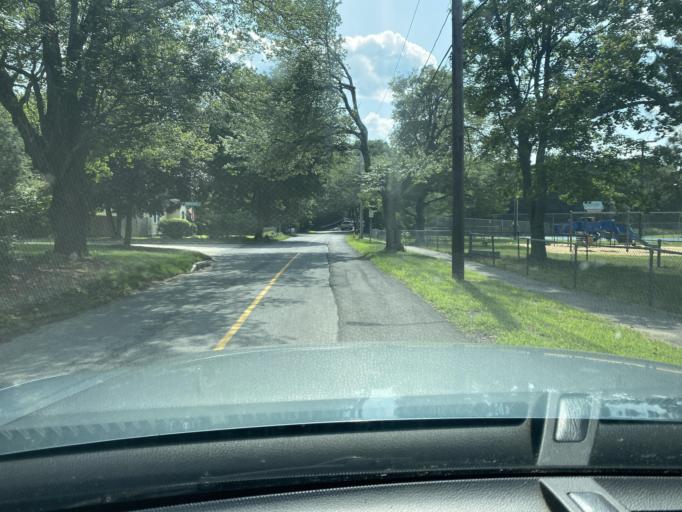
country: US
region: Massachusetts
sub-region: Norfolk County
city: Medfield
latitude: 42.1806
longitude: -71.2989
